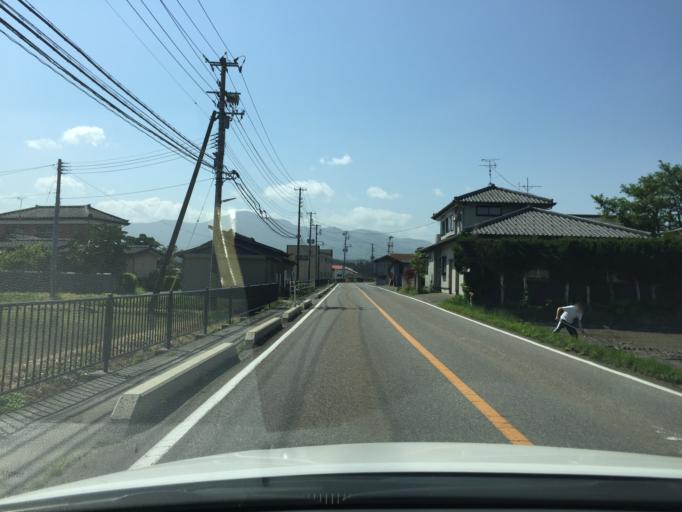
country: JP
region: Niigata
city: Muramatsu
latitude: 37.6852
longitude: 139.1518
